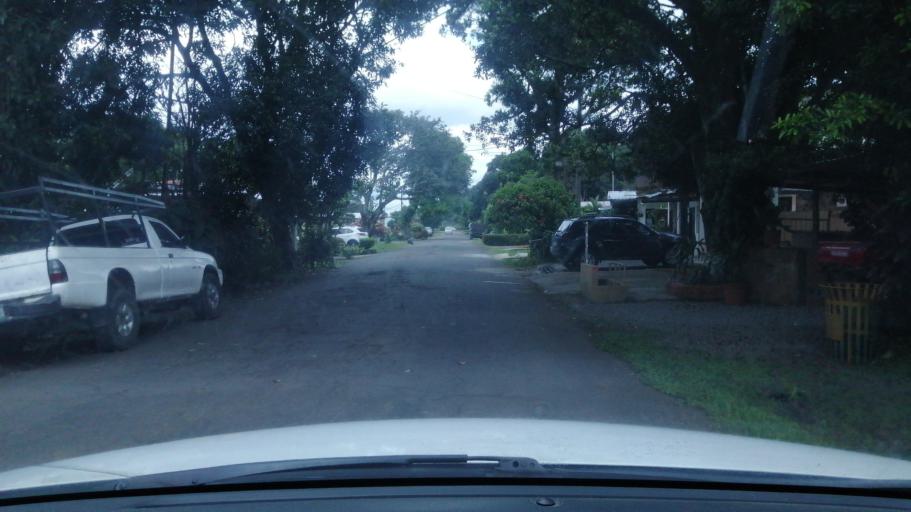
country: PA
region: Chiriqui
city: David
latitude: 8.4435
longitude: -82.4278
